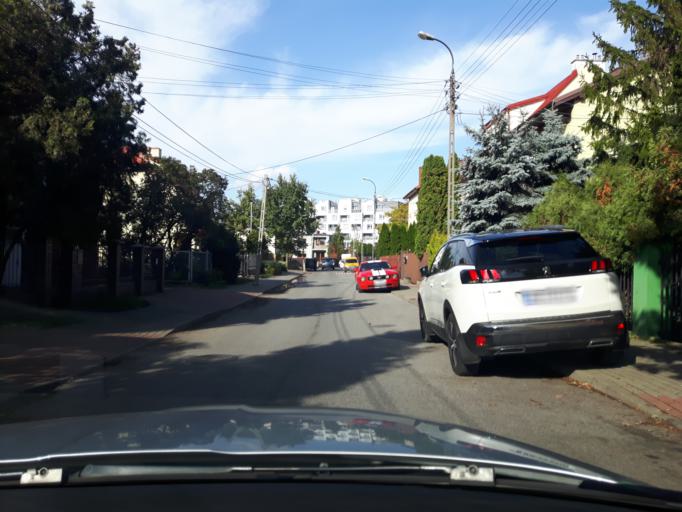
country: PL
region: Masovian Voivodeship
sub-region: Powiat wolominski
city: Zabki
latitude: 52.2854
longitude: 21.0799
